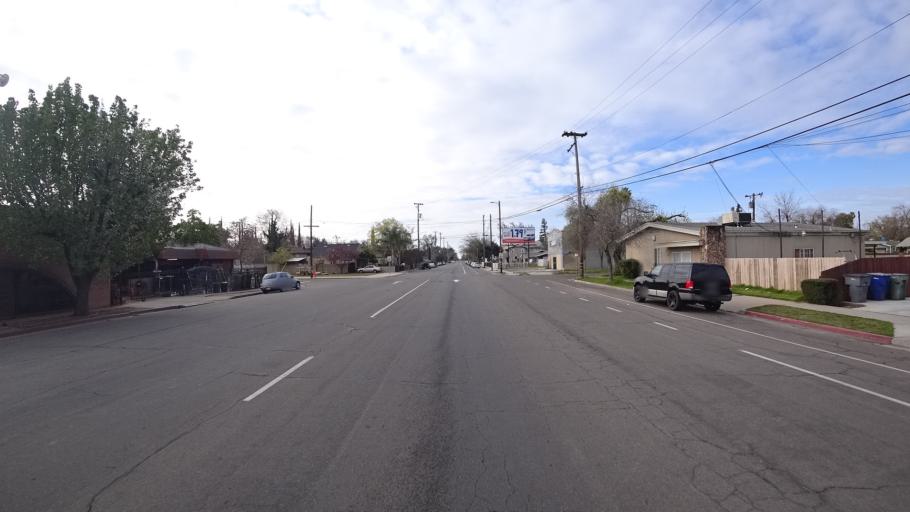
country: US
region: California
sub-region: Fresno County
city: Fresno
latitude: 36.7763
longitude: -119.8011
